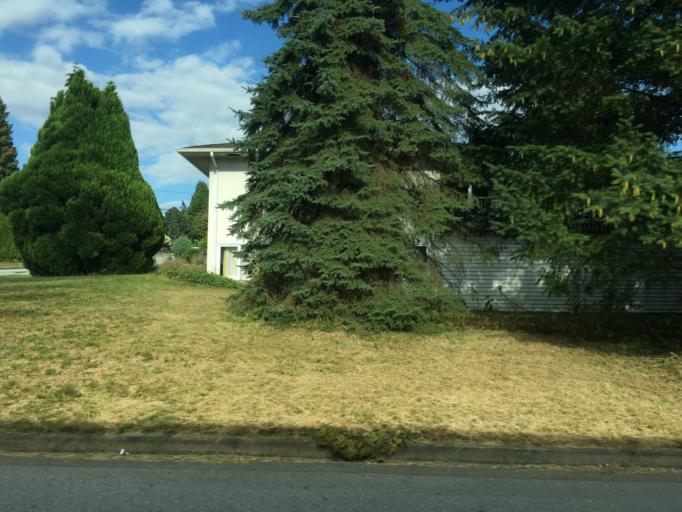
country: CA
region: British Columbia
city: New Westminster
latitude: 49.2471
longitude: -122.8854
